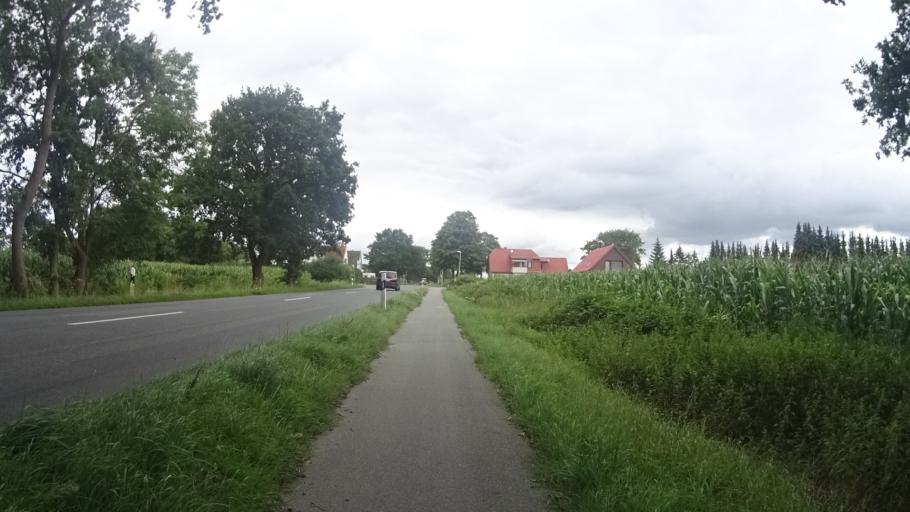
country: DE
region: Lower Saxony
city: Schiffdorf
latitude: 53.5371
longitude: 8.6713
